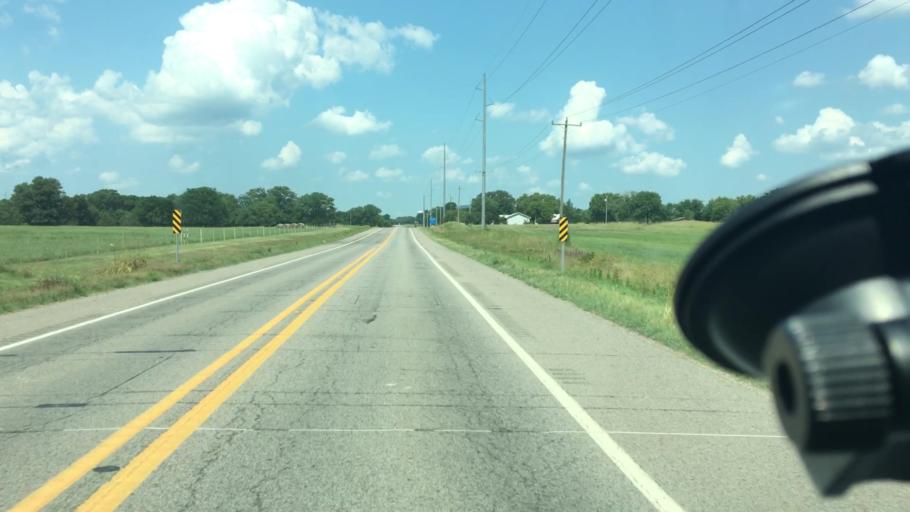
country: US
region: Arkansas
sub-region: Logan County
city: Paris
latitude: 35.2949
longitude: -93.6707
